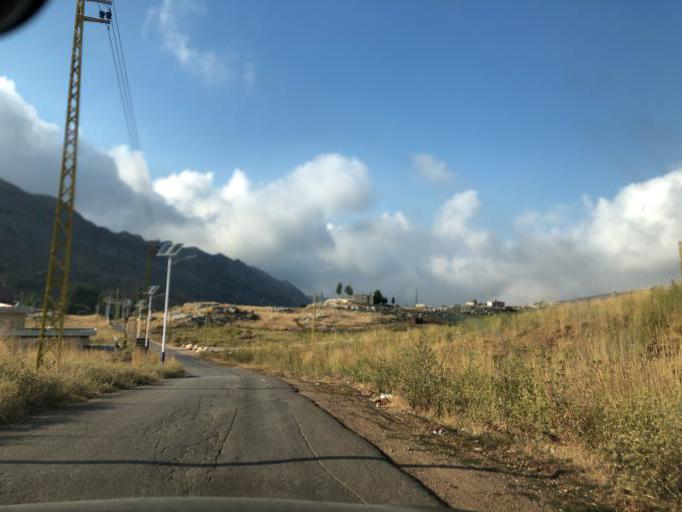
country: LB
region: Liban-Nord
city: Amioun
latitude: 34.1424
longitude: 35.8595
